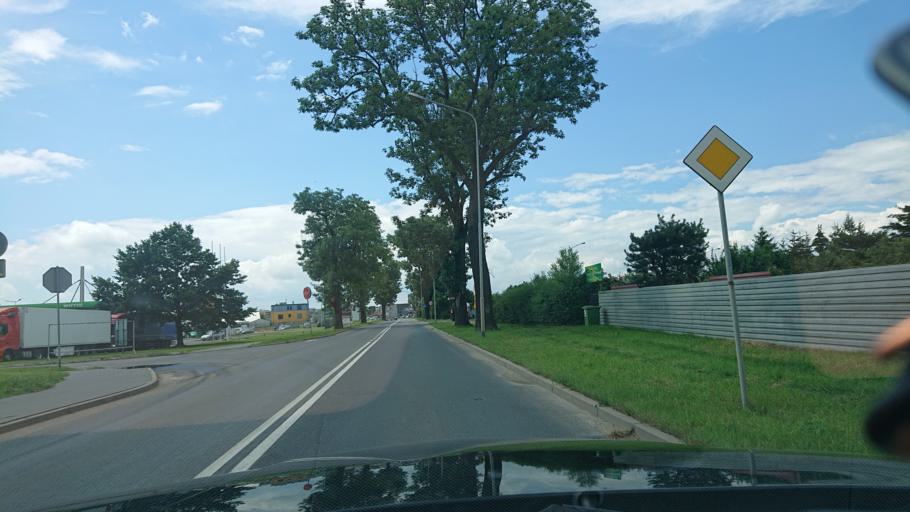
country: PL
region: Greater Poland Voivodeship
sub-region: Powiat gnieznienski
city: Gniezno
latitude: 52.5415
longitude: 17.6332
